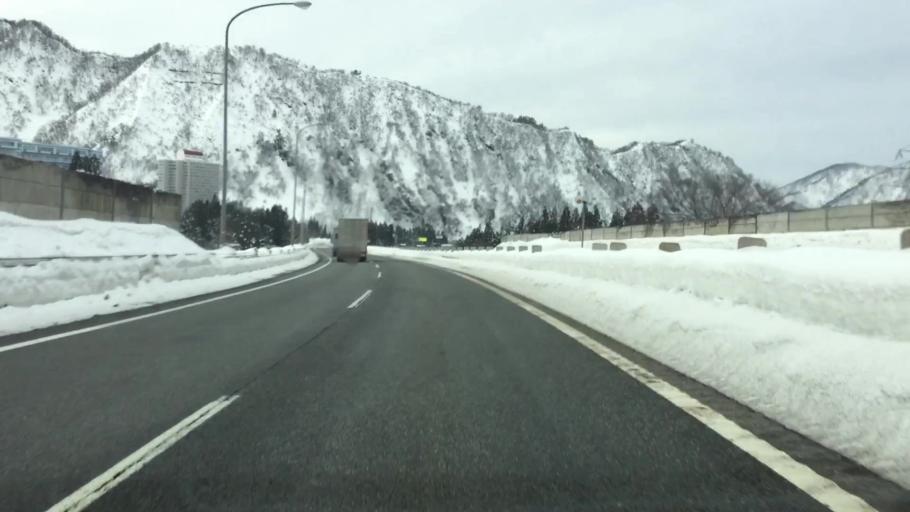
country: JP
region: Niigata
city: Shiozawa
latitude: 36.9062
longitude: 138.8455
